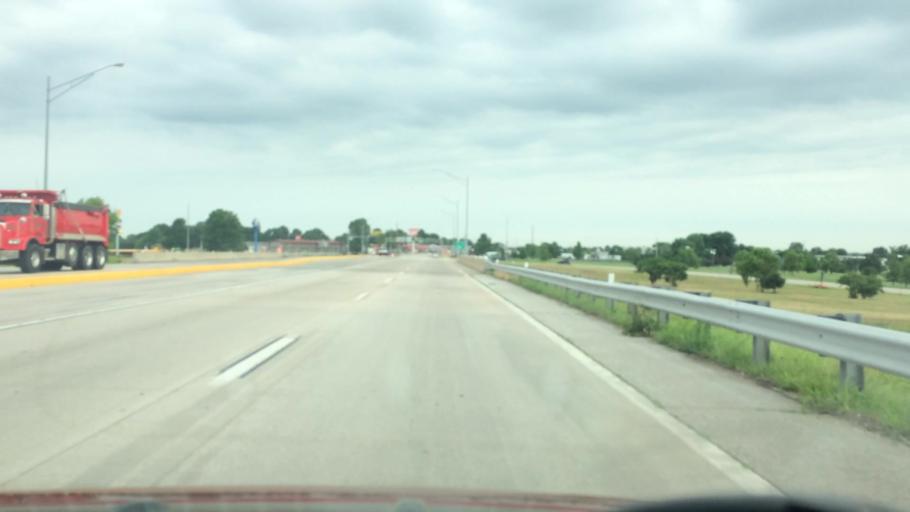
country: US
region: Missouri
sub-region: Greene County
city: Springfield
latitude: 37.2496
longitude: -93.2620
